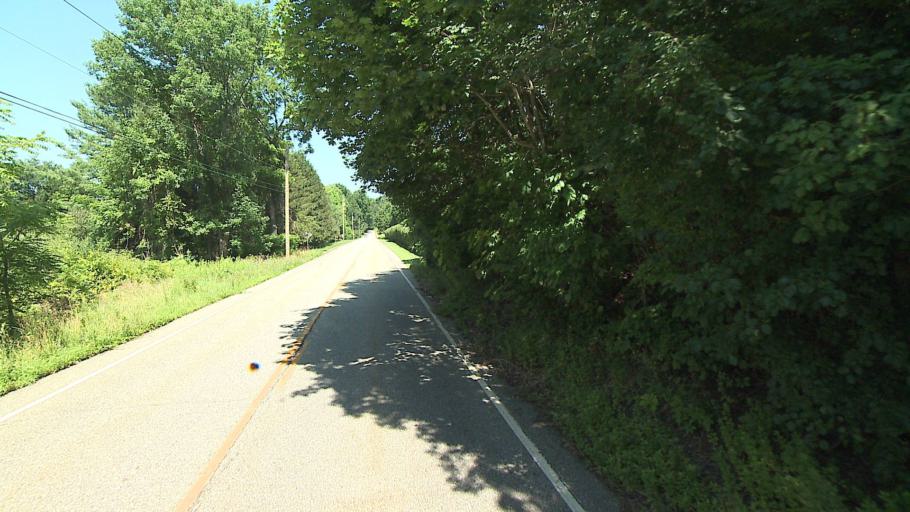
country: US
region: New York
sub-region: Dutchess County
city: Pine Plains
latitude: 41.9179
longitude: -73.4906
